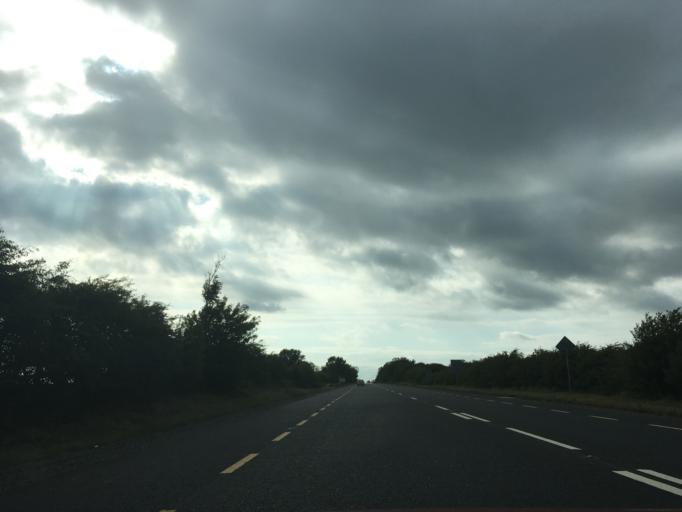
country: IE
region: Leinster
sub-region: Loch Garman
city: Loch Garman
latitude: 52.3407
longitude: -6.5689
